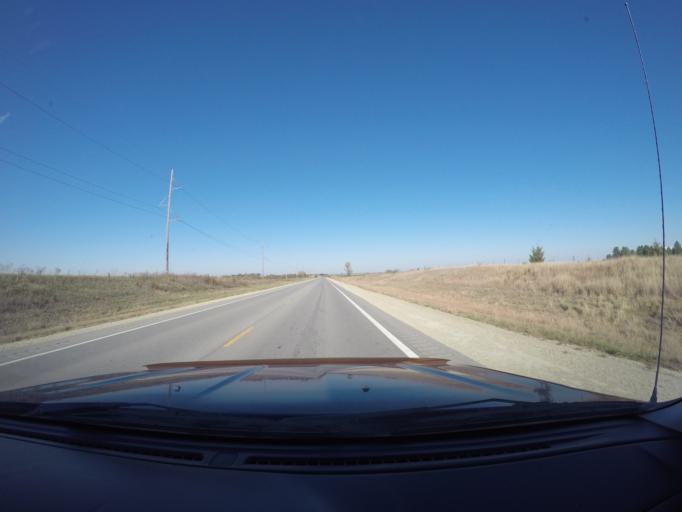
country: US
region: Kansas
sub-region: Riley County
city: Manhattan
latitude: 39.2658
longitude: -96.6843
